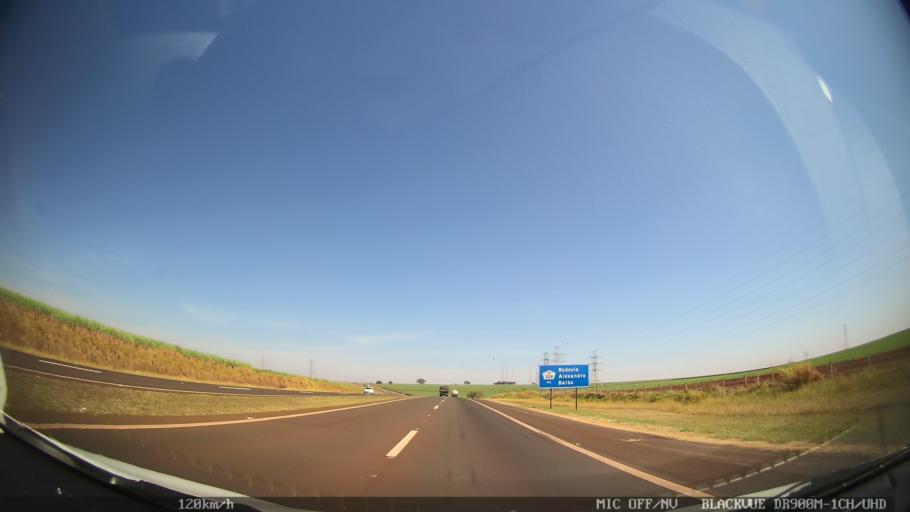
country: BR
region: Sao Paulo
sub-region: Ribeirao Preto
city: Ribeirao Preto
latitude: -21.1519
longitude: -47.8871
